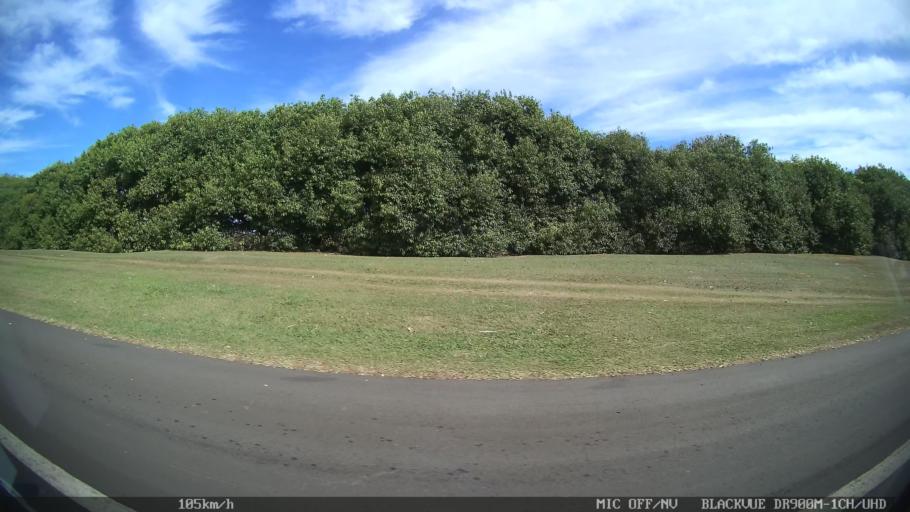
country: BR
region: Sao Paulo
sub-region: Matao
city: Matao
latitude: -21.6693
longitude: -48.3635
